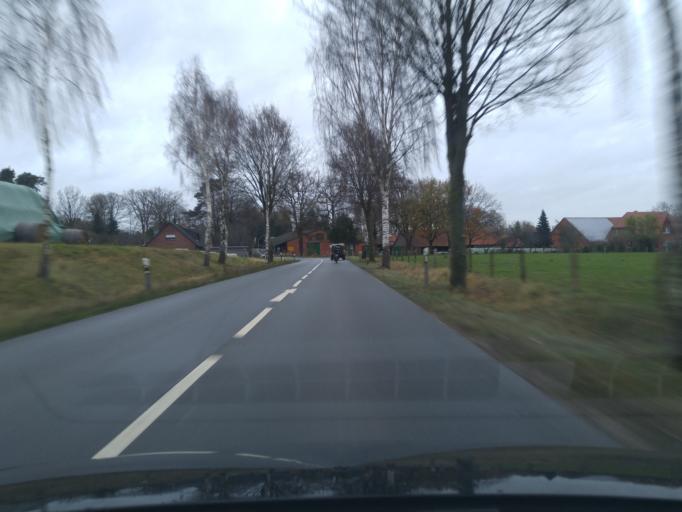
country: DE
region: Lower Saxony
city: Rullstorf
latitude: 53.2657
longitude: 10.5194
